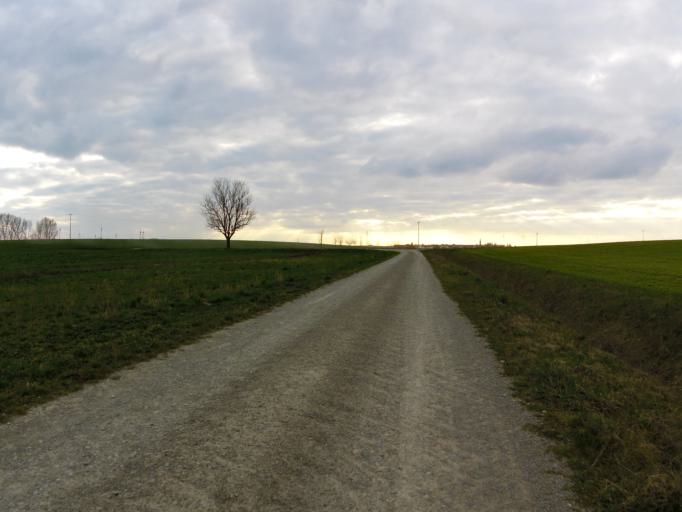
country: DE
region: Bavaria
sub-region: Regierungsbezirk Unterfranken
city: Biebelried
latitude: 49.7449
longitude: 10.0886
